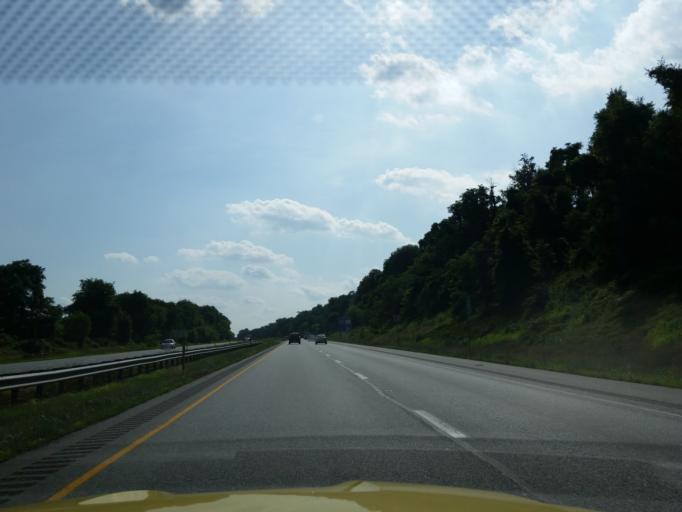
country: US
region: Pennsylvania
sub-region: York County
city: Wrightsville
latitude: 40.0333
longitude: -76.5365
